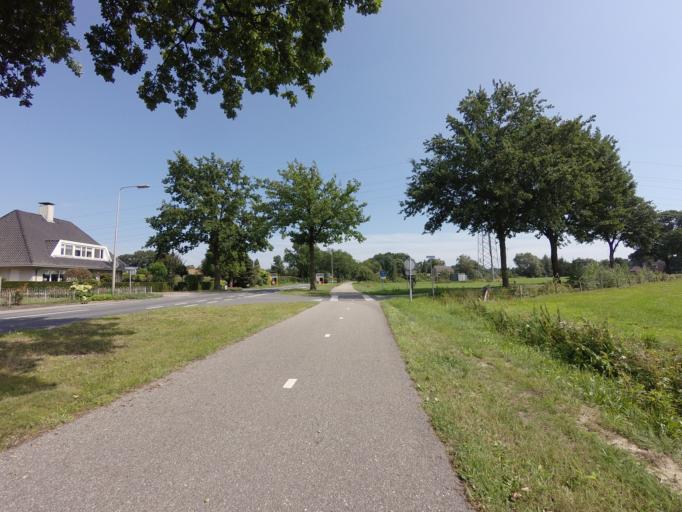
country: NL
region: Overijssel
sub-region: Gemeente Hof van Twente
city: Hengevelde
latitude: 52.2004
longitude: 6.6483
